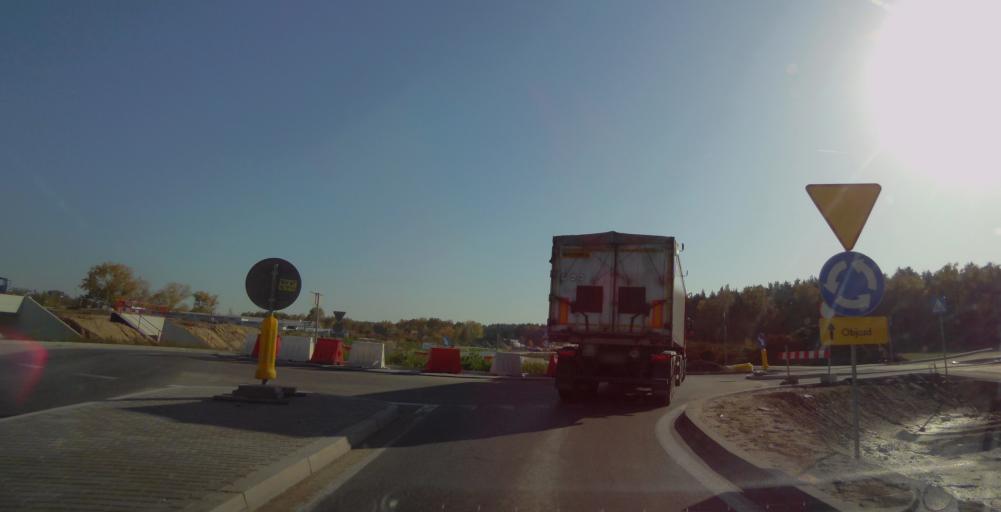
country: PL
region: Masovian Voivodeship
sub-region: Powiat otwocki
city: Jozefow
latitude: 52.1828
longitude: 21.2849
